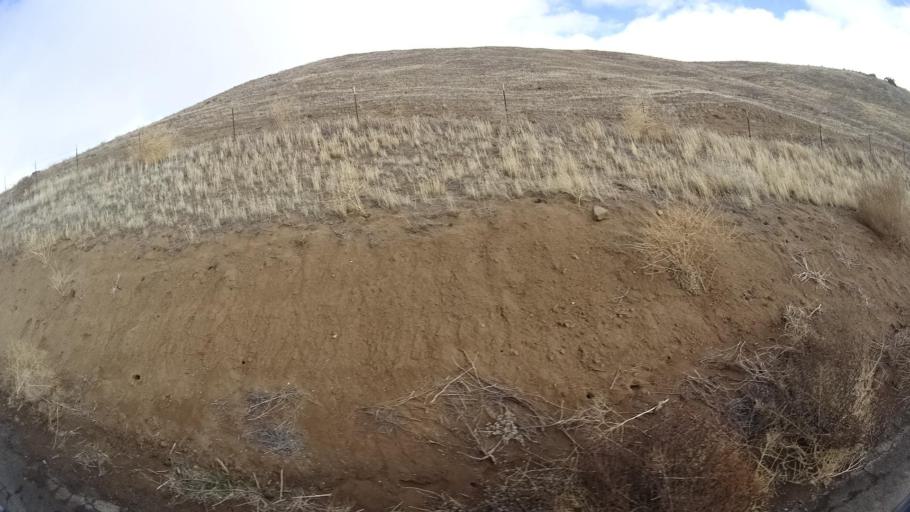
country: US
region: California
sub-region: Kern County
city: Maricopa
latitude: 34.9125
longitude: -119.3977
